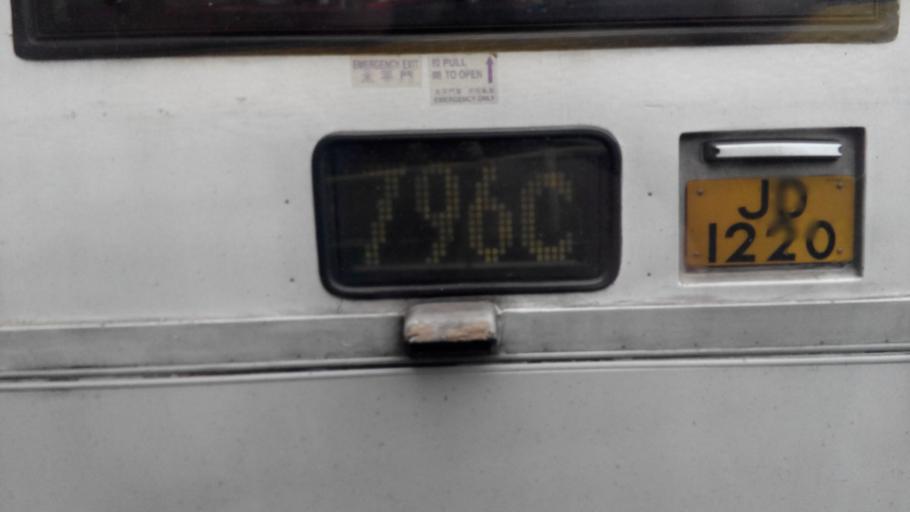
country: HK
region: Sham Shui Po
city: Sham Shui Po
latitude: 22.3376
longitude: 114.1593
